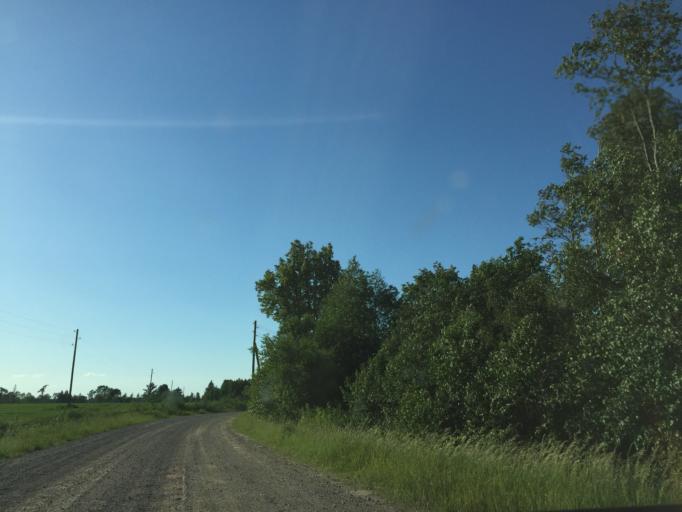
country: LV
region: Kandava
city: Kandava
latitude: 56.8513
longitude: 22.6946
